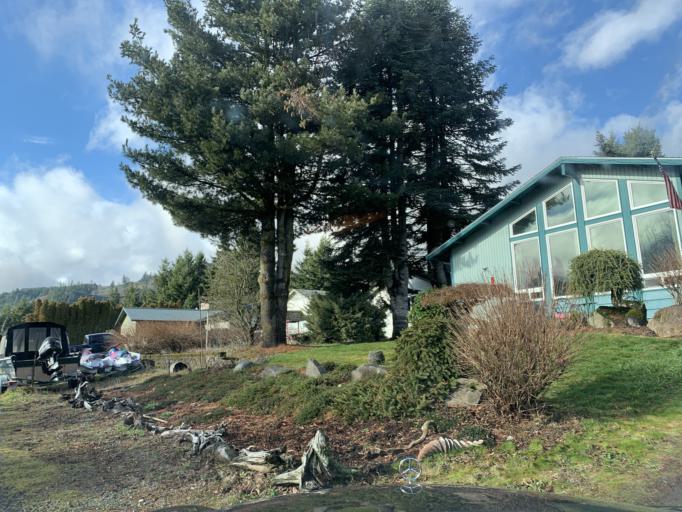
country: US
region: Washington
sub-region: Skamania County
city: Carson
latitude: 45.7203
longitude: -121.8157
